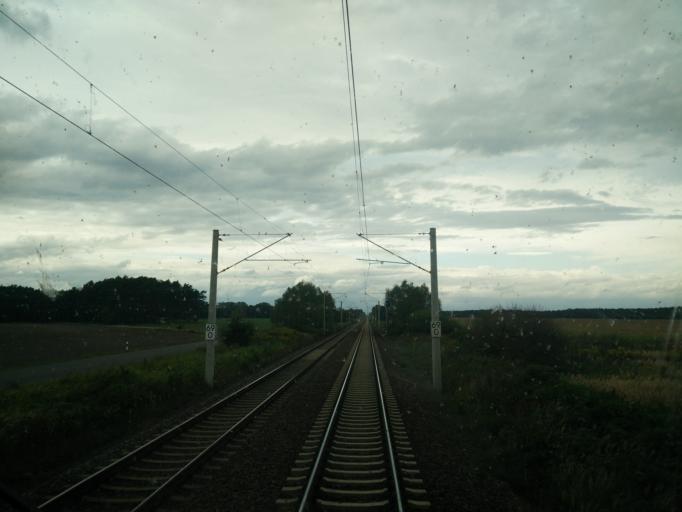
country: DE
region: Brandenburg
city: Luebben
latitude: 51.9683
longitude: 13.8124
